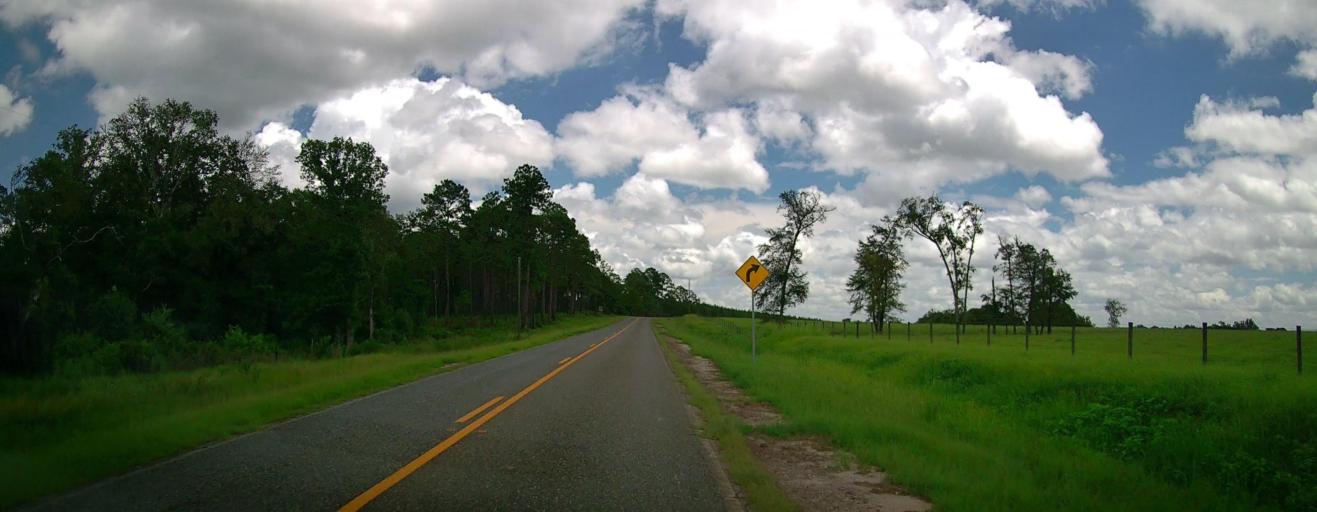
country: US
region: Georgia
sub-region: Turner County
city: Ashburn
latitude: 31.6980
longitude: -83.4889
